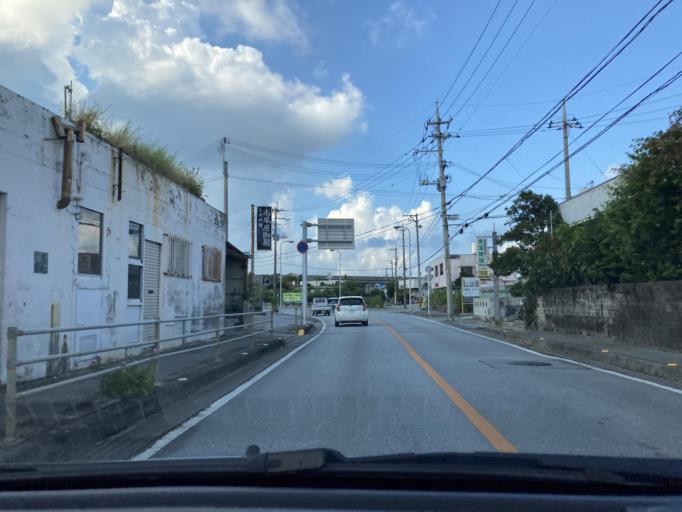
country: JP
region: Okinawa
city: Tomigusuku
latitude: 26.1829
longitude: 127.7258
